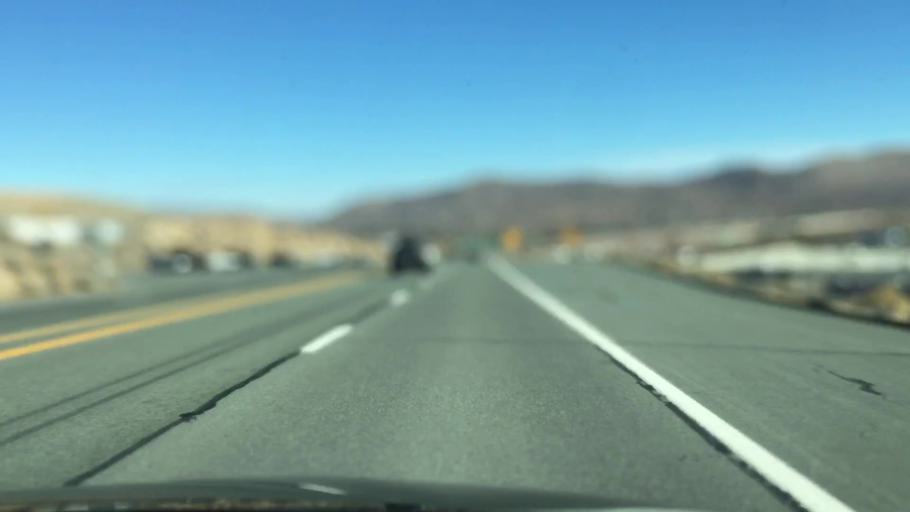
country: US
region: Nevada
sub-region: Douglas County
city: Indian Hills
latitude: 39.1163
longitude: -119.7806
